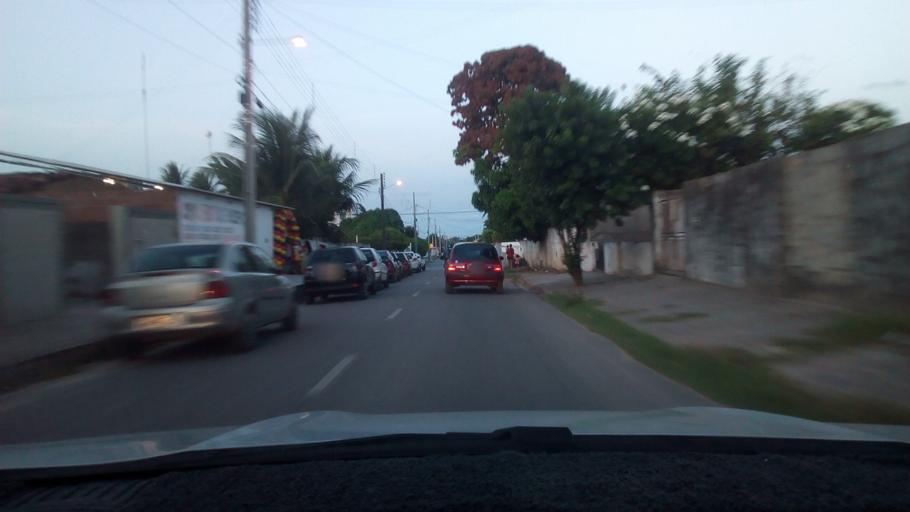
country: BR
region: Paraiba
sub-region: Bayeux
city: Bayeux
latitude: -7.1767
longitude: -34.9181
